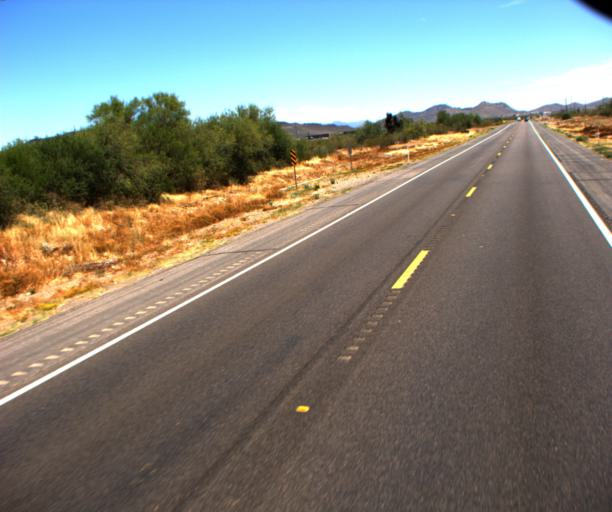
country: US
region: Arizona
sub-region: Maricopa County
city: Anthem
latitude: 33.7981
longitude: -112.1775
